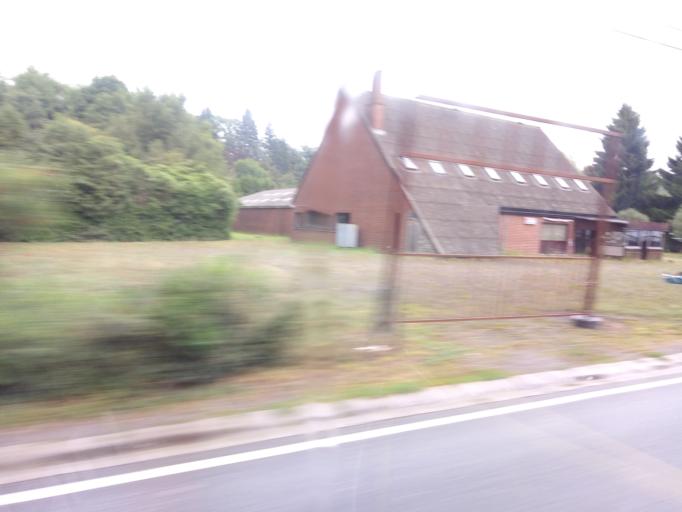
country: BE
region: Wallonia
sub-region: Province du Luxembourg
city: Hotton
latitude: 50.2597
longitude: 5.4670
